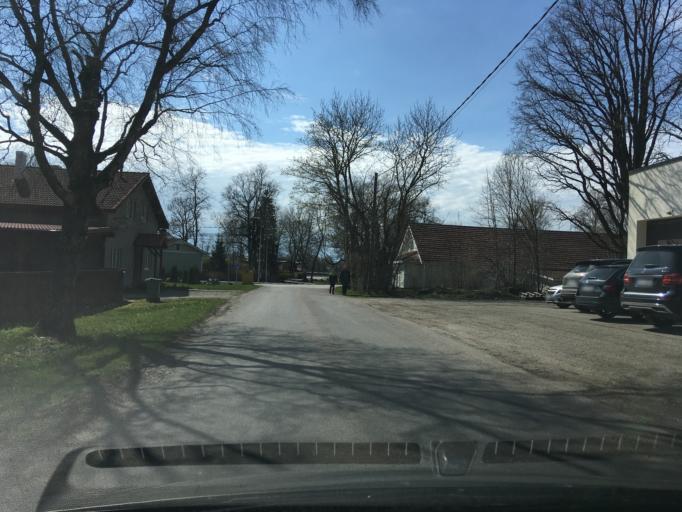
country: EE
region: Harju
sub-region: Raasiku vald
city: Raasiku
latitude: 59.3666
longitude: 25.1776
